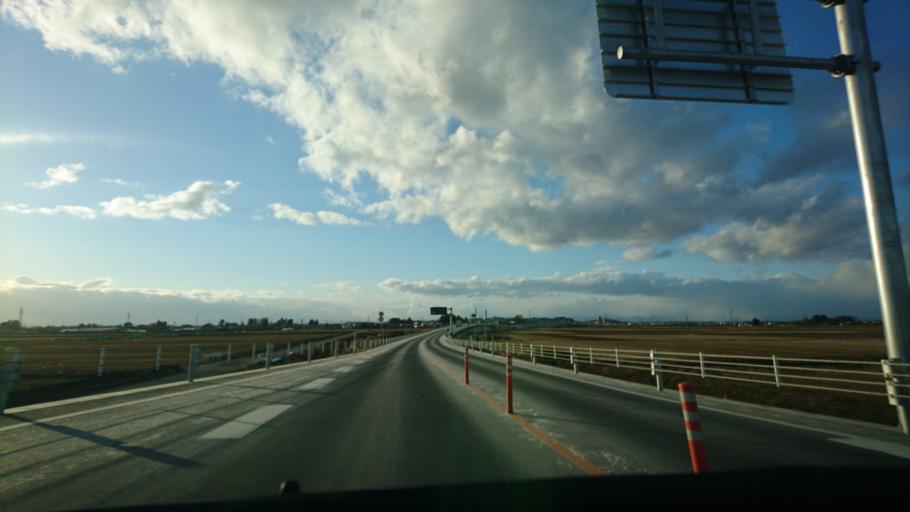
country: JP
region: Miyagi
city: Wakuya
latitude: 38.6864
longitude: 141.2300
